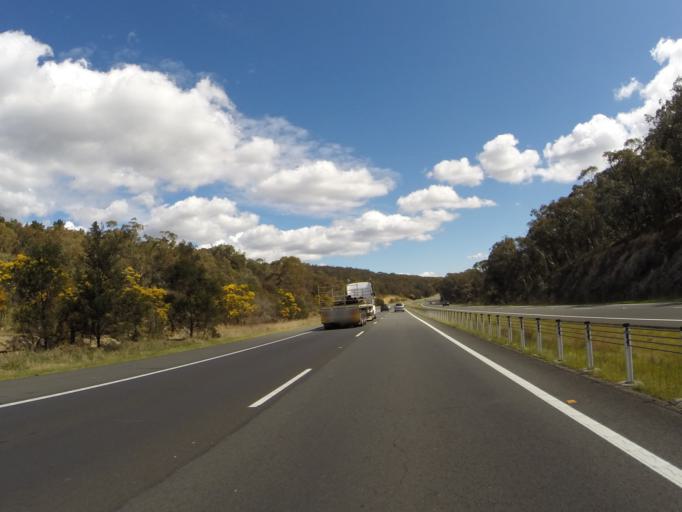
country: AU
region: New South Wales
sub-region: Goulburn Mulwaree
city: Goulburn
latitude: -34.7441
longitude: 149.9300
